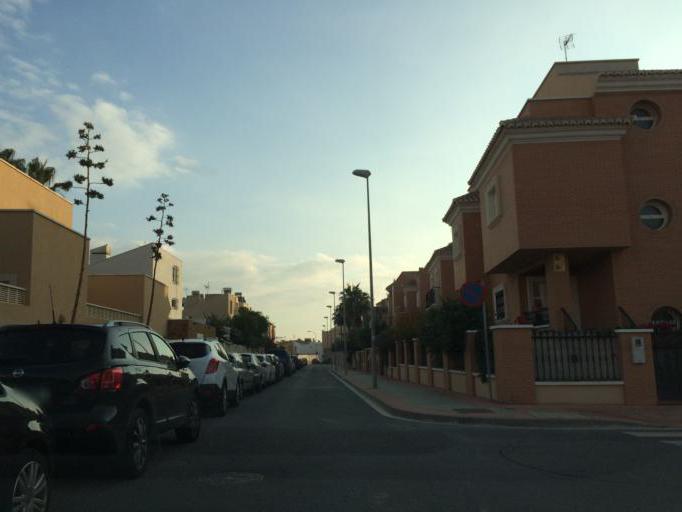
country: ES
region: Andalusia
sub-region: Provincia de Almeria
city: Almeria
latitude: 36.8230
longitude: -2.4372
